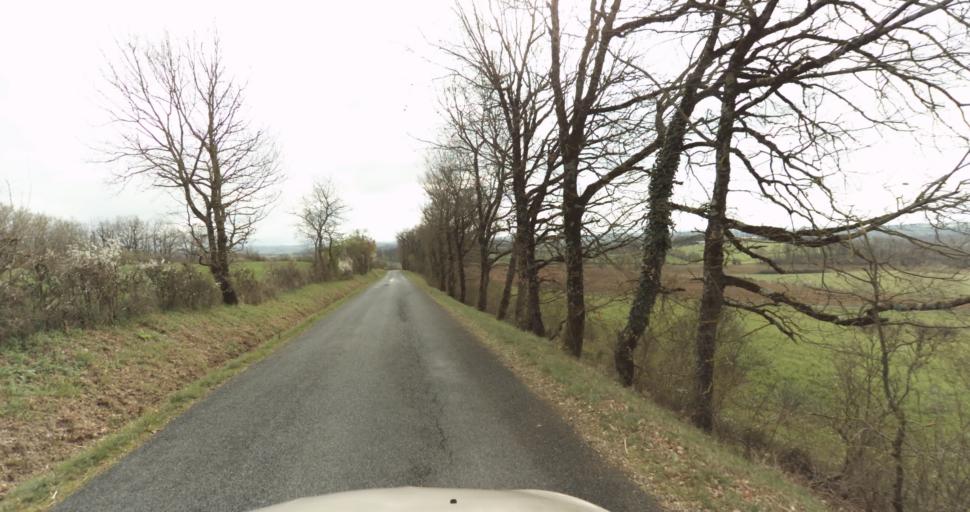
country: FR
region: Midi-Pyrenees
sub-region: Departement du Tarn
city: Frejairolles
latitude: 43.8659
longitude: 2.2127
